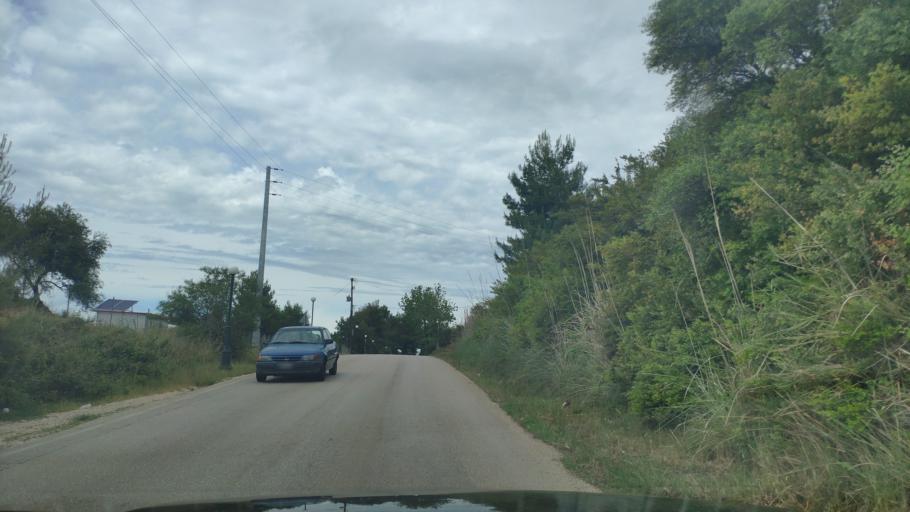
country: GR
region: West Greece
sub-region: Nomos Aitolias kai Akarnanias
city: Palairos
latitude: 38.7750
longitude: 20.8822
